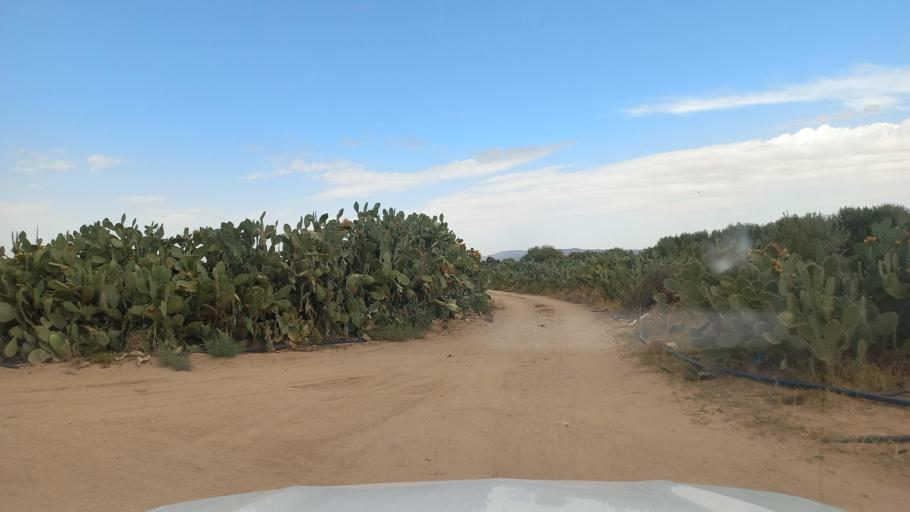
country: TN
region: Al Qasrayn
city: Kasserine
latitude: 35.2365
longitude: 9.0167
